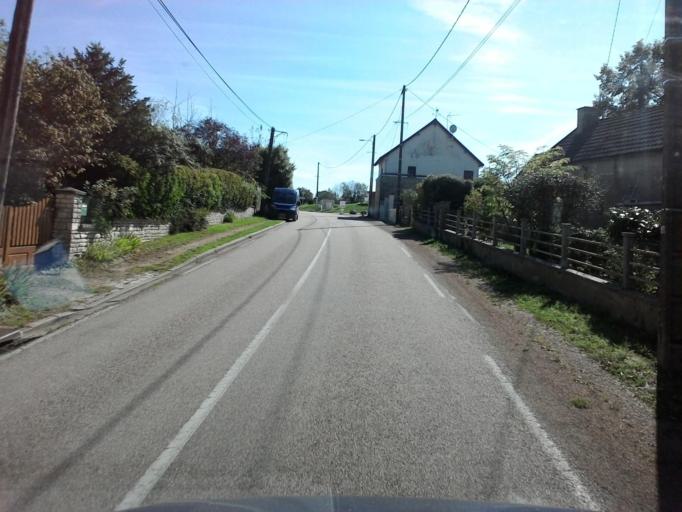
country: FR
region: Bourgogne
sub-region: Departement de l'Yonne
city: Joux-la-Ville
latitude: 47.6088
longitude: 3.8631
